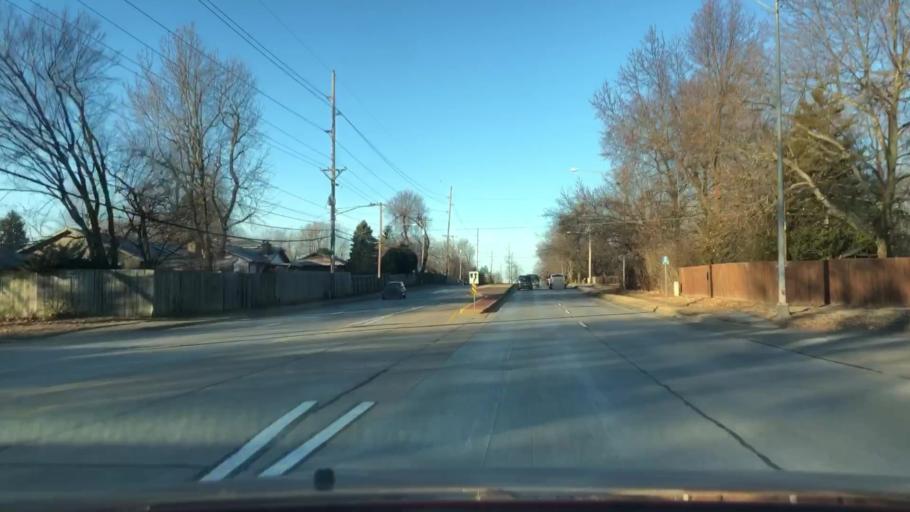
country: US
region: Missouri
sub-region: Greene County
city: Springfield
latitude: 37.1588
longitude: -93.2496
